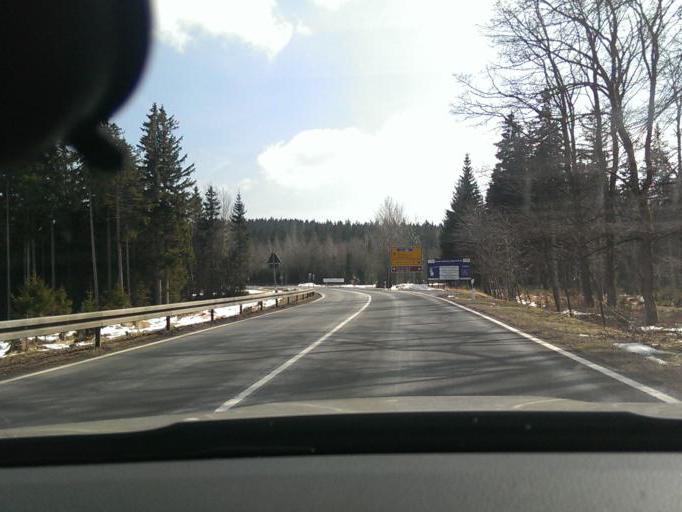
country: DE
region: Thuringia
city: Oberhof
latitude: 50.7191
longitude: 10.7235
